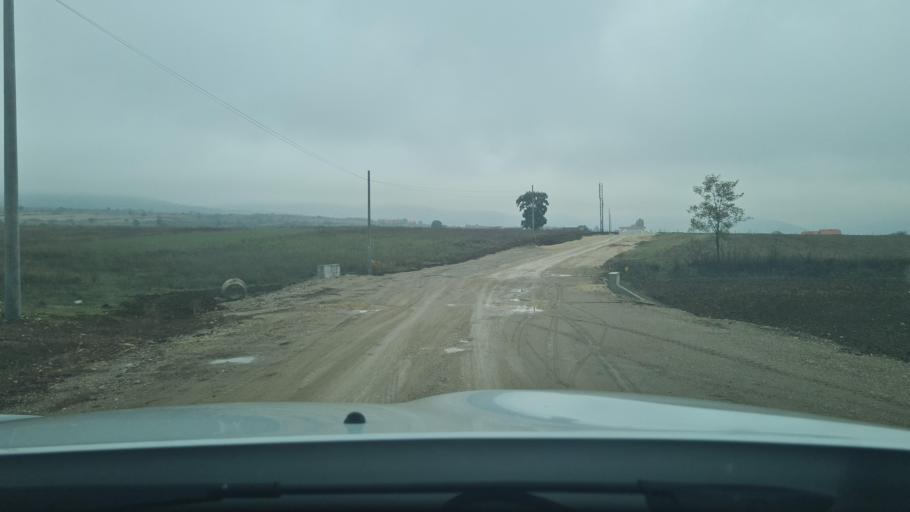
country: MK
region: Opstina Lipkovo
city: Matejche
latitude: 42.1135
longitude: 21.6110
